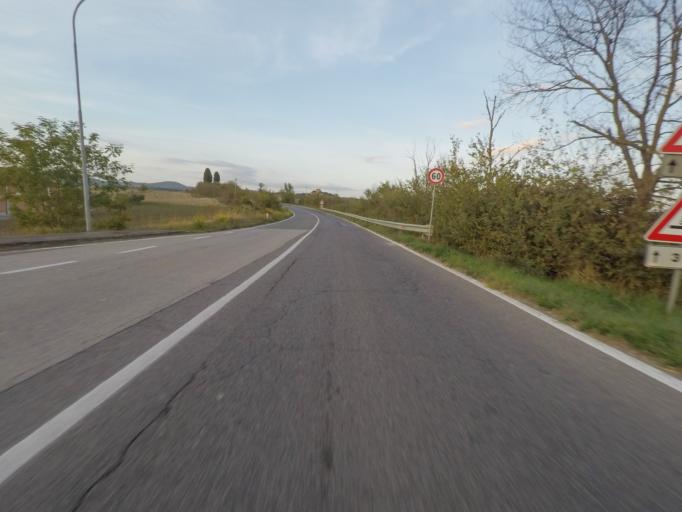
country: IT
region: Tuscany
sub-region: Provincia di Siena
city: Pienza
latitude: 43.0929
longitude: 11.6885
